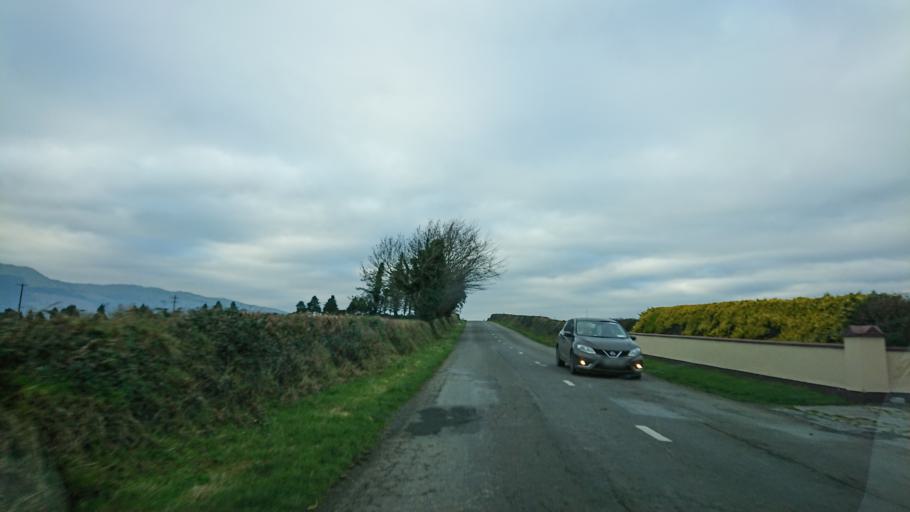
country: IE
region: Munster
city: Carrick-on-Suir
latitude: 52.3025
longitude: -7.4865
